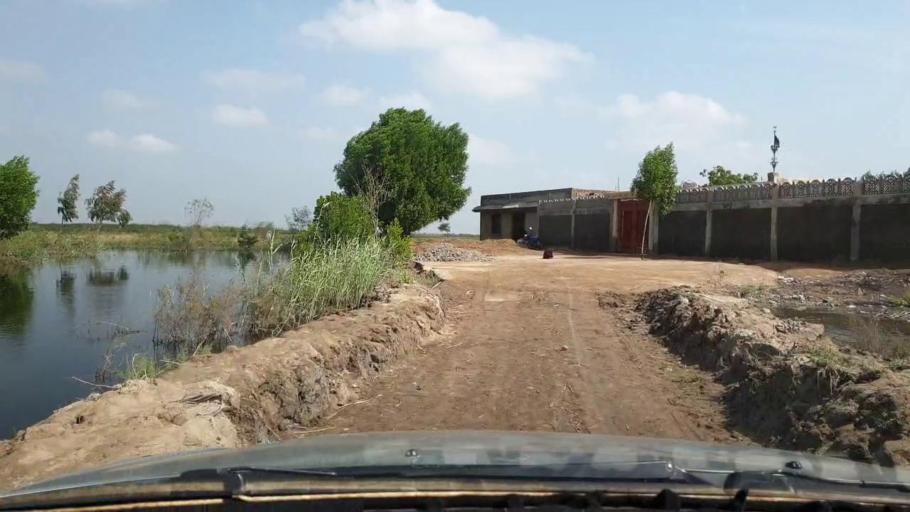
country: PK
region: Sindh
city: Matli
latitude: 25.1016
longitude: 68.6684
